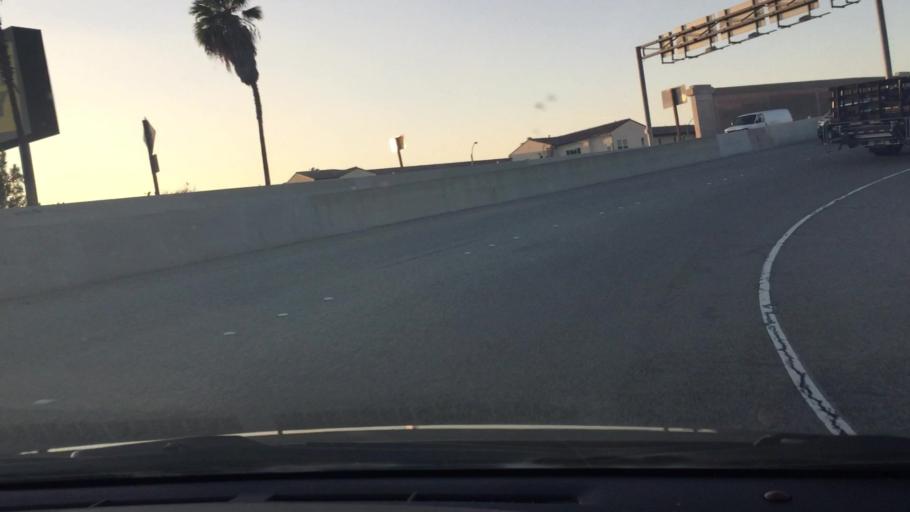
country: US
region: California
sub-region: Orange County
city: Orange
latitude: 33.7914
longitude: -117.8917
